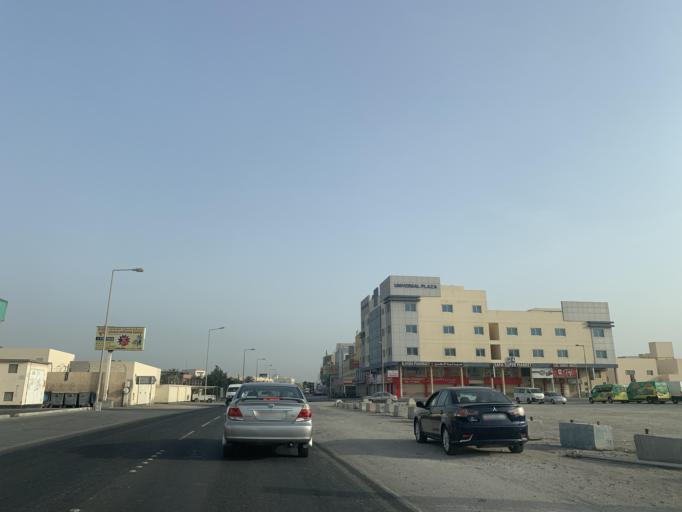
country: BH
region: Northern
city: Madinat `Isa
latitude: 26.1871
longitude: 50.5575
